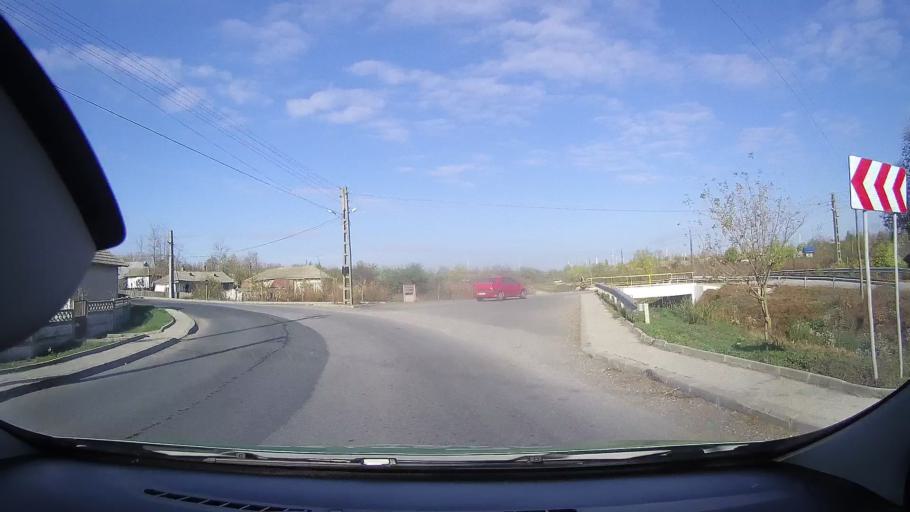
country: RO
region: Tulcea
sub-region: Comuna Valea Nucarilor
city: Valea Nucarilor
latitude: 45.0425
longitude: 28.9353
